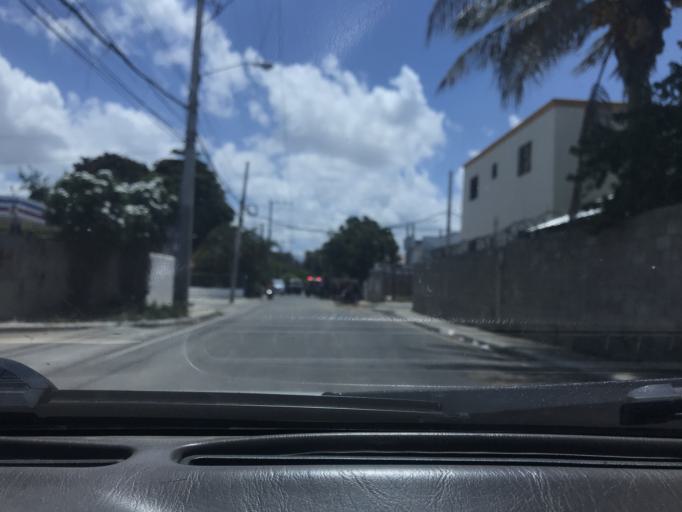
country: DO
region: Santiago
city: Santiago de los Caballeros
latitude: 19.4218
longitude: -70.7070
